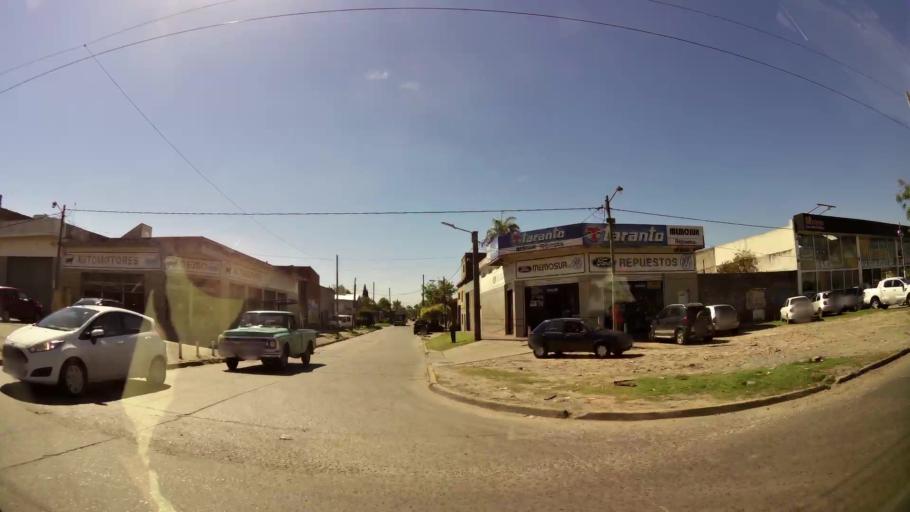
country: AR
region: Buenos Aires
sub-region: Partido de Almirante Brown
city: Adrogue
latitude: -34.7589
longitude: -58.3564
